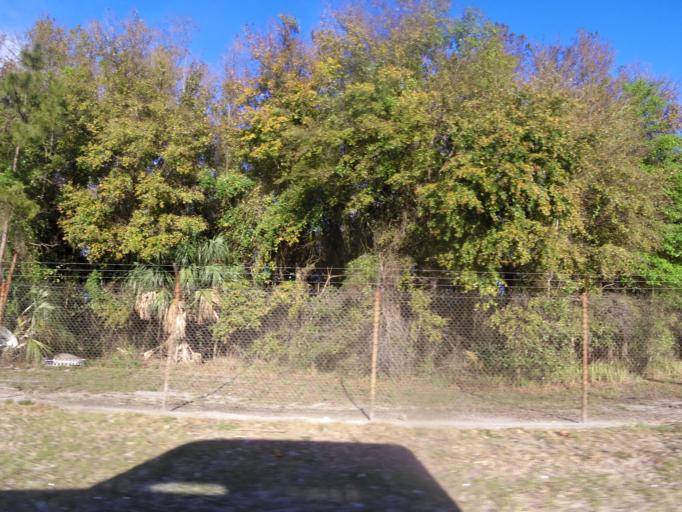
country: US
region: Florida
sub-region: Duval County
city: Jacksonville
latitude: 30.4221
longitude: -81.6010
